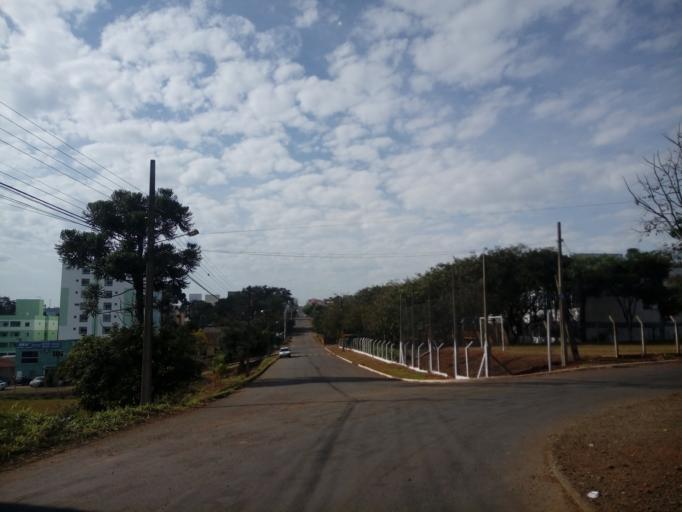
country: BR
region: Santa Catarina
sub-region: Chapeco
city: Chapeco
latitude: -27.1186
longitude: -52.6285
